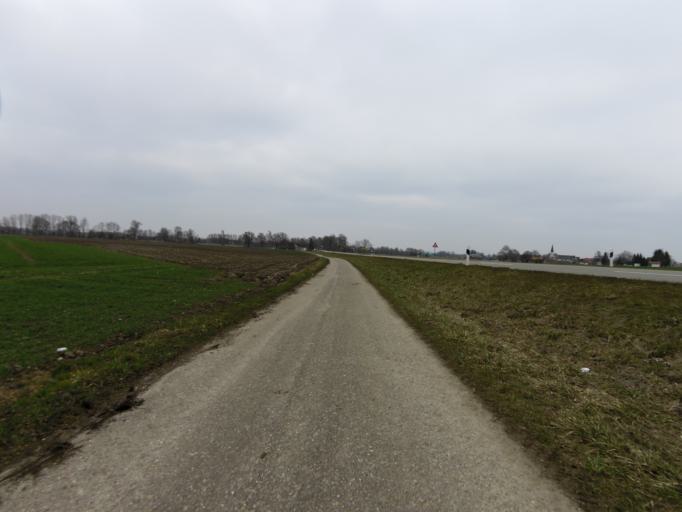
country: DE
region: Bavaria
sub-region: Upper Bavaria
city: Berglern
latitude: 48.4129
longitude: 11.9290
